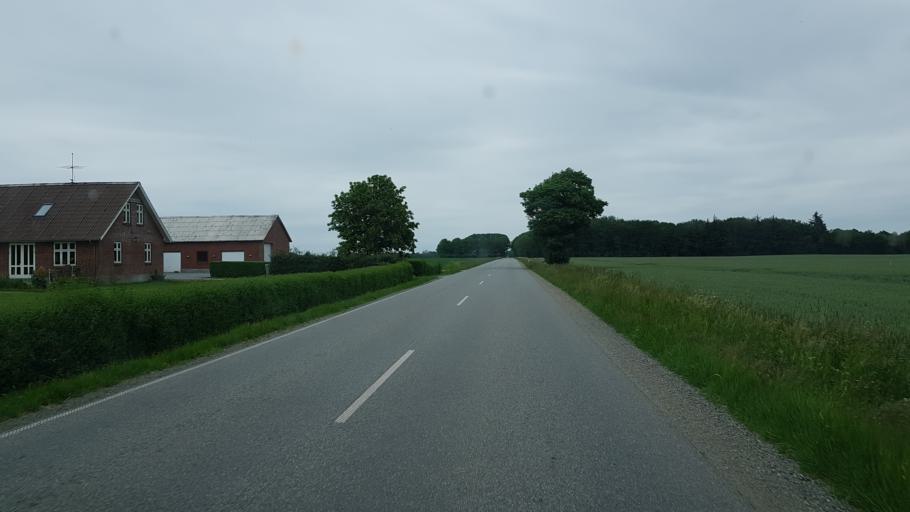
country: DK
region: South Denmark
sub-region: Varde Kommune
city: Olgod
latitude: 55.7167
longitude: 8.7058
